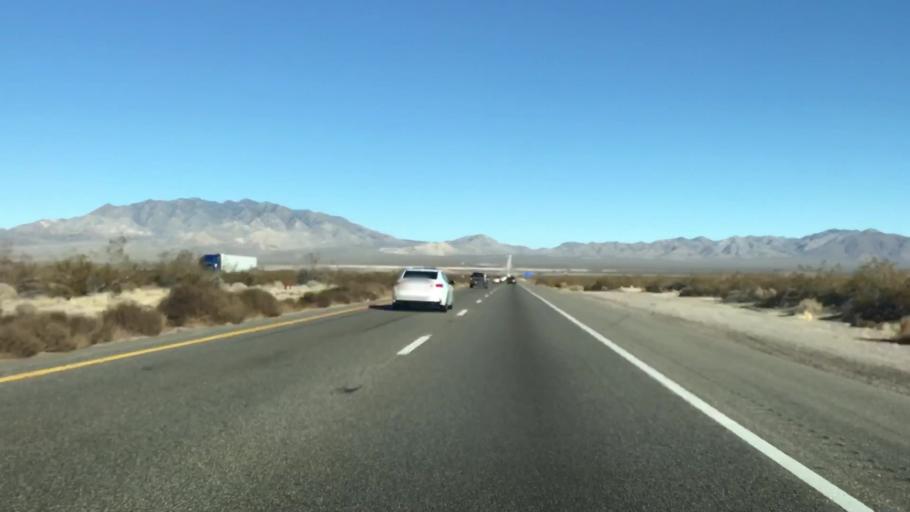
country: US
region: Nevada
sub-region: Clark County
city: Sandy Valley
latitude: 35.4215
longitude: -115.7402
